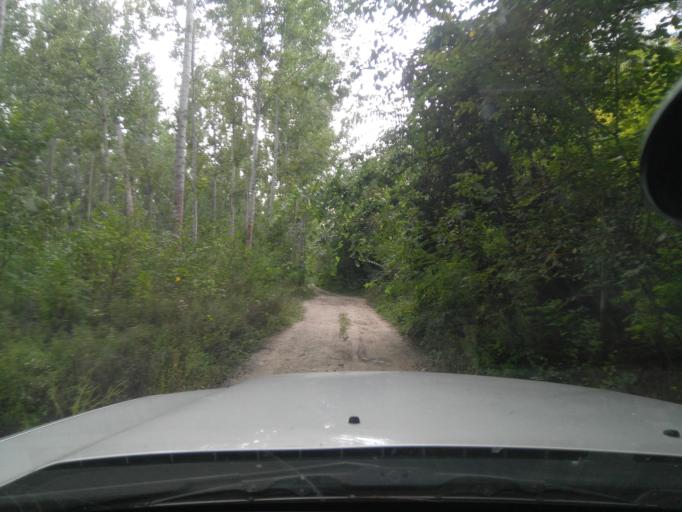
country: HU
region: Bacs-Kiskun
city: Apostag
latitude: 46.8942
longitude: 18.9390
